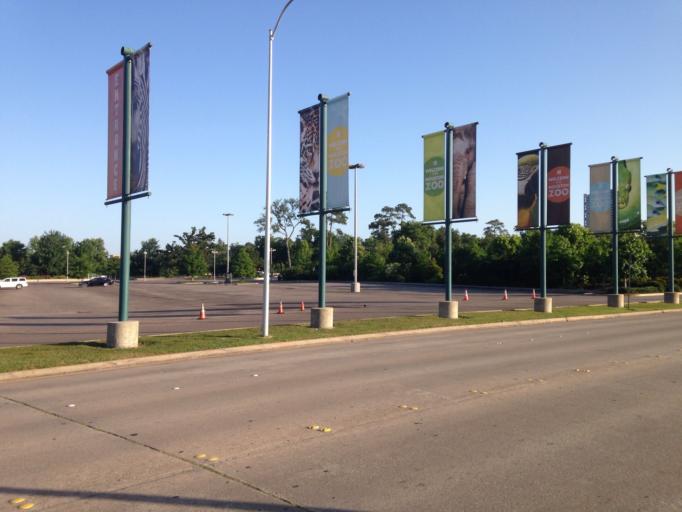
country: US
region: Texas
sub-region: Harris County
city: West University Place
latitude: 29.7155
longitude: -95.3890
